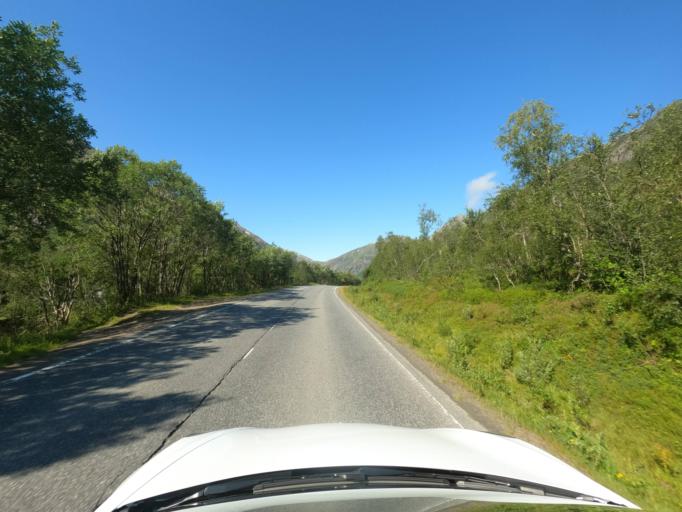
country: NO
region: Nordland
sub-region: Lodingen
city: Lodingen
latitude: 68.5604
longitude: 15.7596
